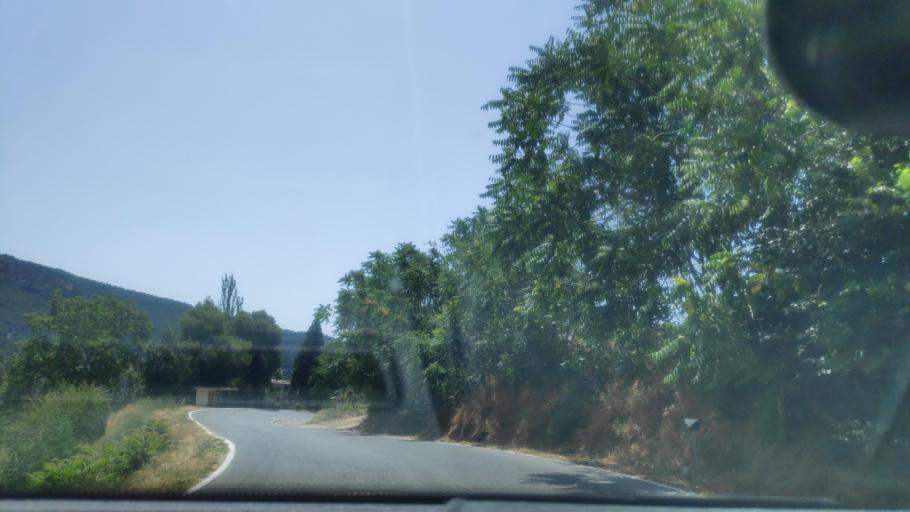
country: ES
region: Andalusia
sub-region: Provincia de Granada
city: Busquistar
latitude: 36.9609
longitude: -3.2791
